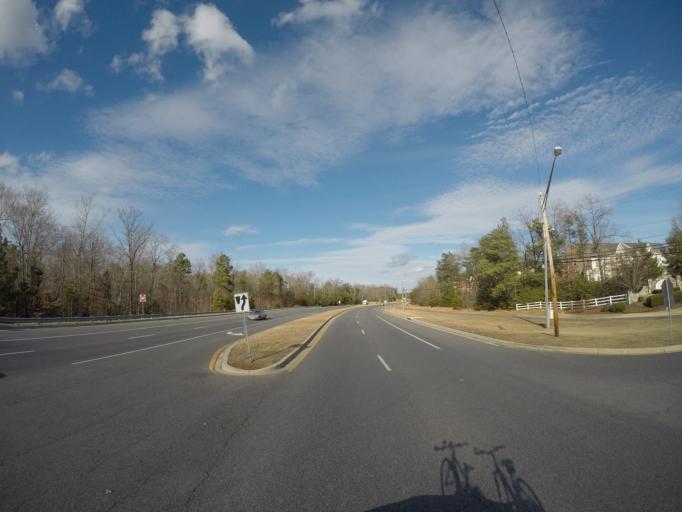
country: US
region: Maryland
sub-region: Charles County
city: Waldorf
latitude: 38.6281
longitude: -76.9681
